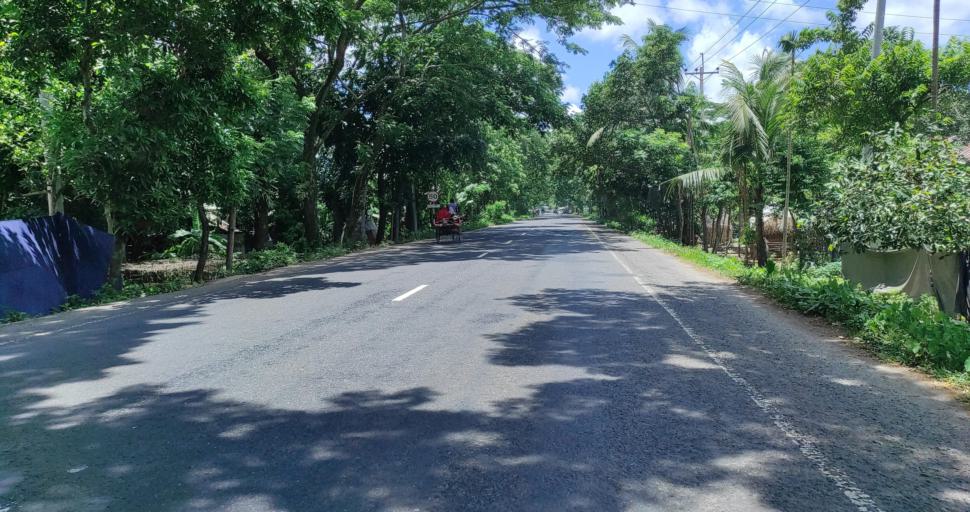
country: BD
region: Barisal
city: Barisal
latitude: 22.8198
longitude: 90.2702
